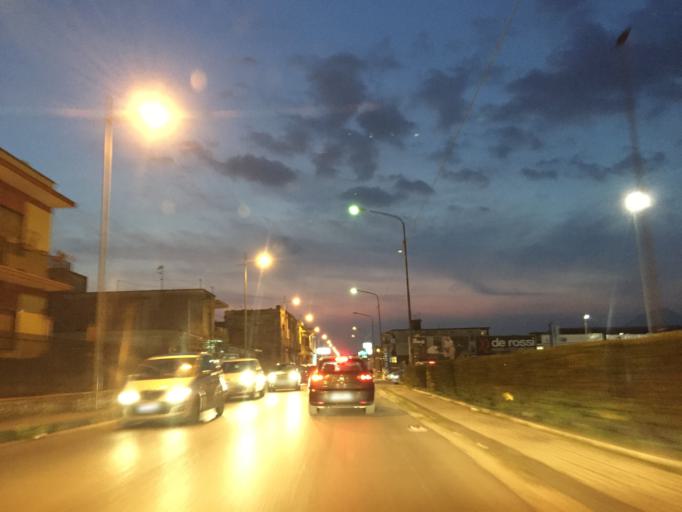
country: IT
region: Campania
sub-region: Provincia di Salerno
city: Sant'Egidio del Monte Albino
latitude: 40.7478
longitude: 14.5993
